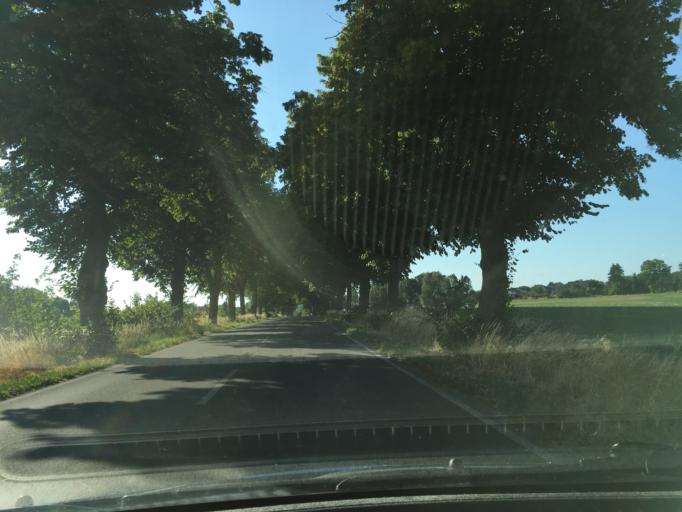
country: DE
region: Lower Saxony
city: Dahlem
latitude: 53.1815
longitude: 10.7573
